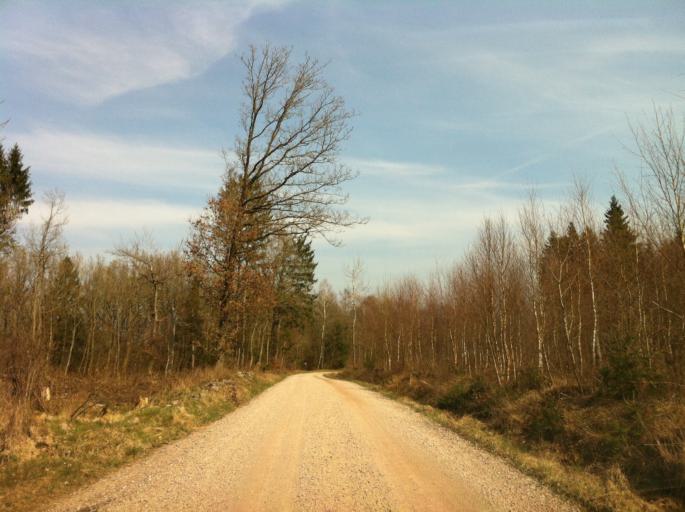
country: SE
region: Skane
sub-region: Eslovs Kommun
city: Stehag
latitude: 55.9993
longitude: 13.3197
